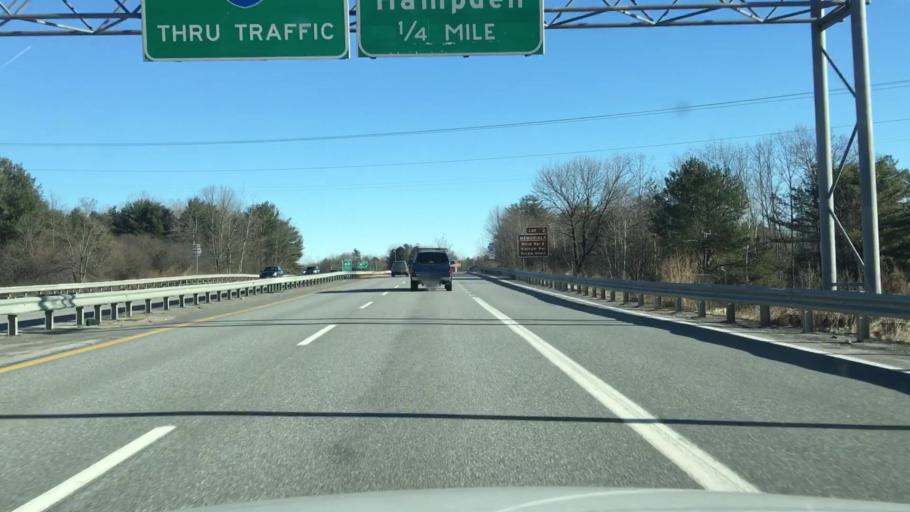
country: US
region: Maine
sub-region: Penobscot County
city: Bangor
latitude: 44.7864
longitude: -68.8033
